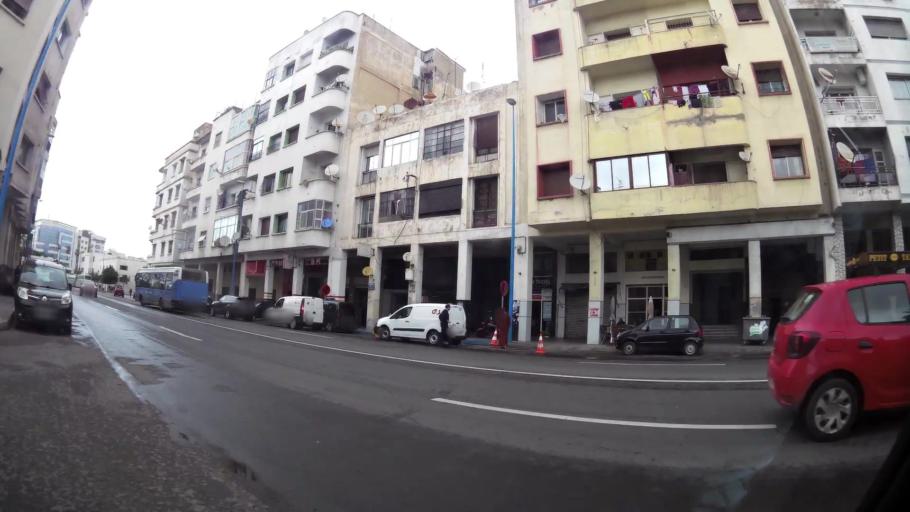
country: MA
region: Grand Casablanca
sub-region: Casablanca
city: Casablanca
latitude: 33.5983
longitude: -7.6306
